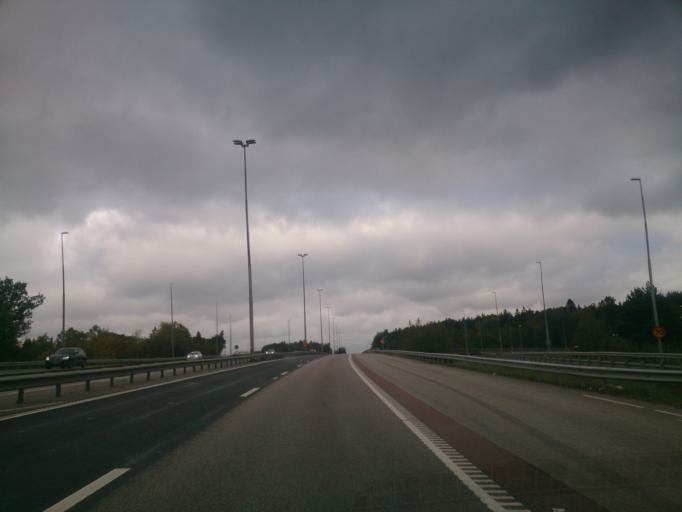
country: SE
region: Stockholm
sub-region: Haninge Kommun
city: Handen
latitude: 59.2272
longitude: 18.1263
